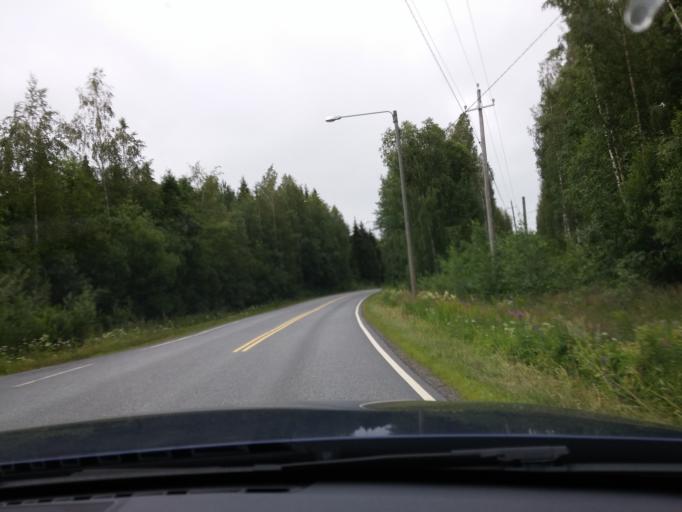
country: FI
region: Central Finland
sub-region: Joutsa
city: Joutsa
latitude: 61.8105
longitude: 25.9692
